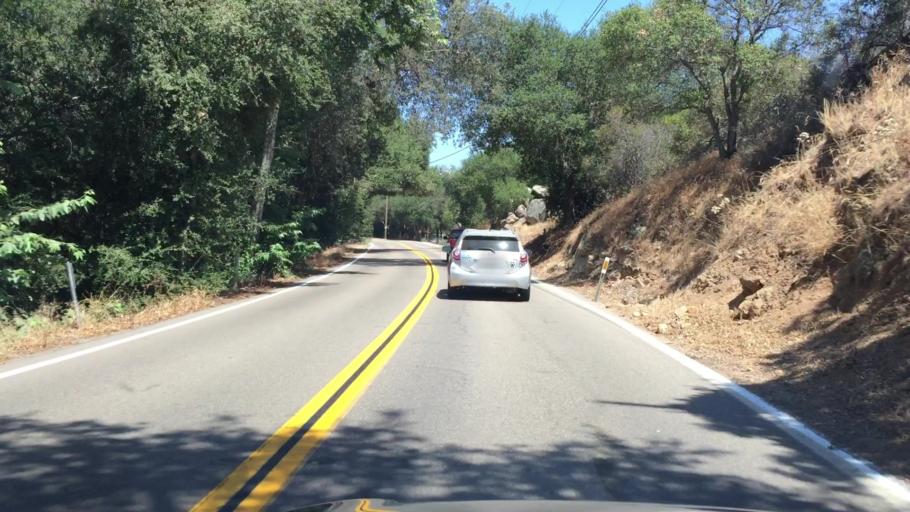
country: US
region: California
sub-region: San Diego County
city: Jamul
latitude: 32.7429
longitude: -116.8100
